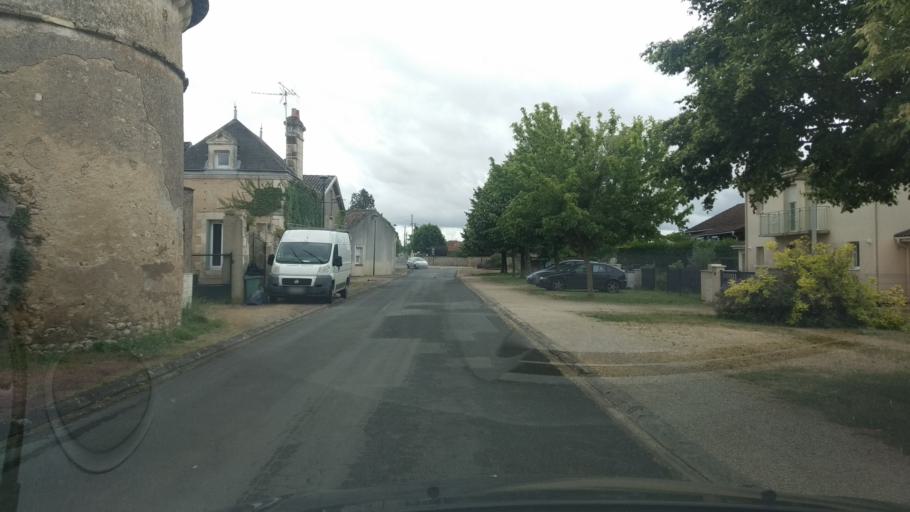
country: FR
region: Poitou-Charentes
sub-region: Departement de la Vienne
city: Vouneuil-sous-Biard
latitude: 46.6057
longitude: 0.2788
